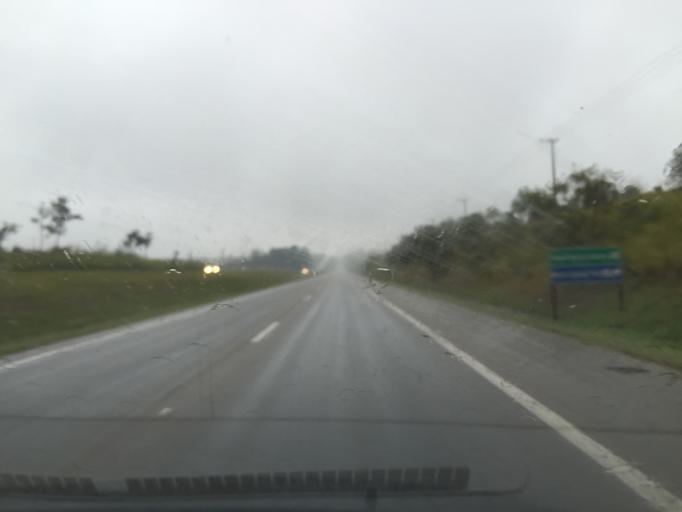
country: BR
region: Sao Paulo
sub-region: Itu
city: Itu
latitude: -23.3379
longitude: -47.3245
